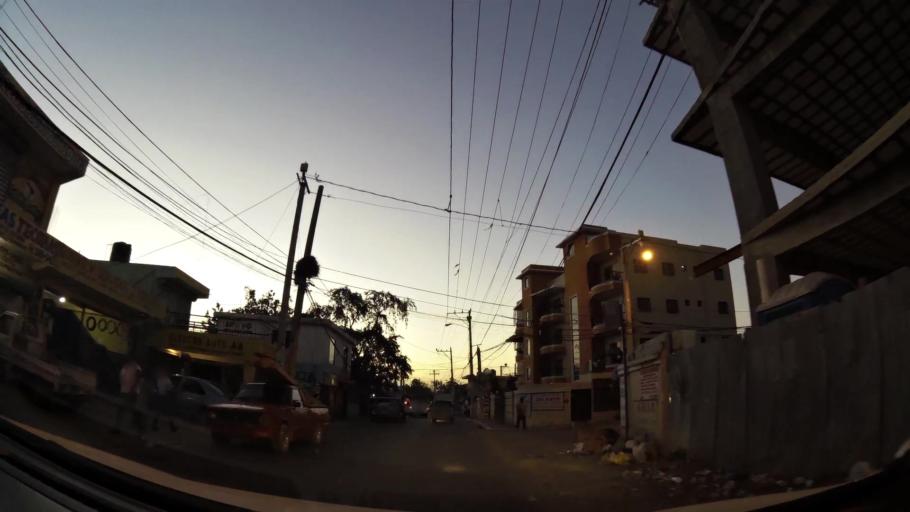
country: DO
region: Santo Domingo
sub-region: Santo Domingo
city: Santo Domingo Este
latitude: 18.5003
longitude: -69.8377
